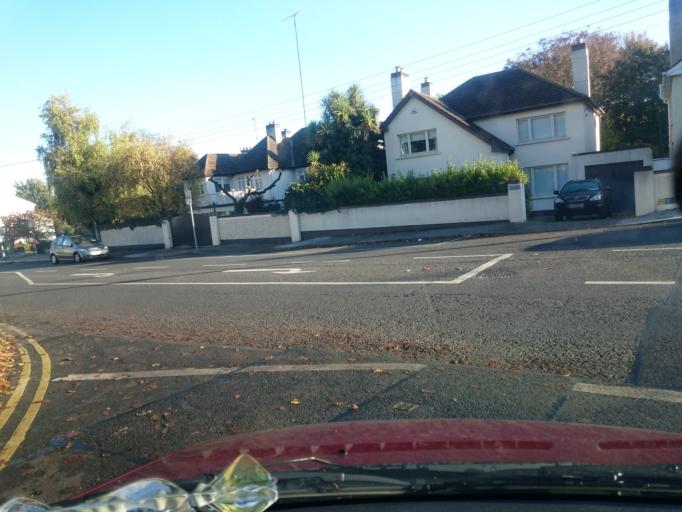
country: IE
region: Leinster
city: Monkstown
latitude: 53.2916
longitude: -6.1515
